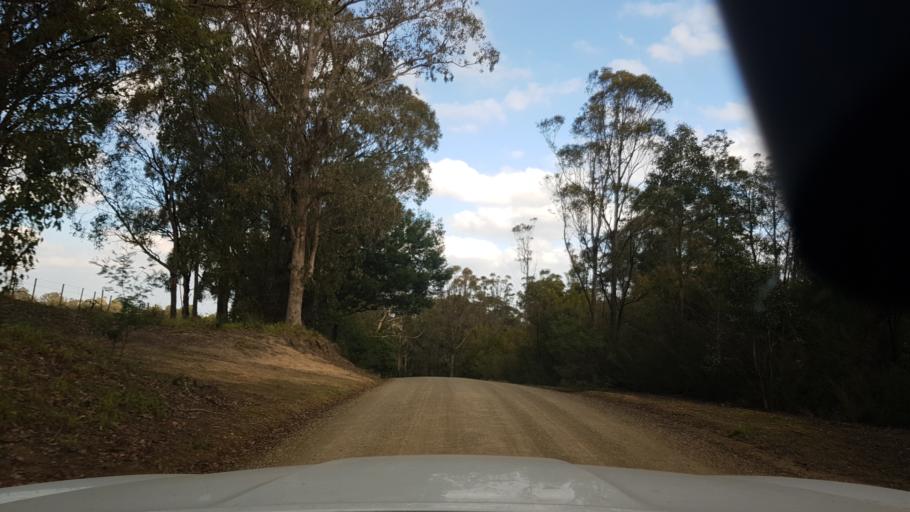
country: AU
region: Victoria
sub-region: East Gippsland
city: Bairnsdale
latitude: -37.7704
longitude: 147.5677
